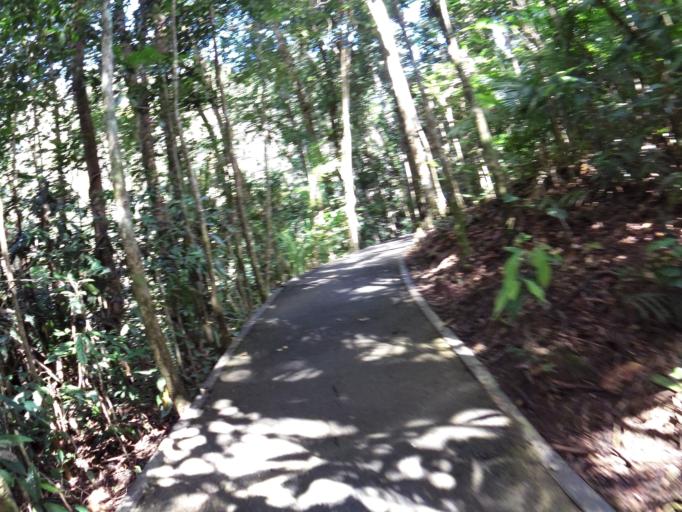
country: AU
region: Queensland
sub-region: Tablelands
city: Kuranda
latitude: -16.8246
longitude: 145.6334
